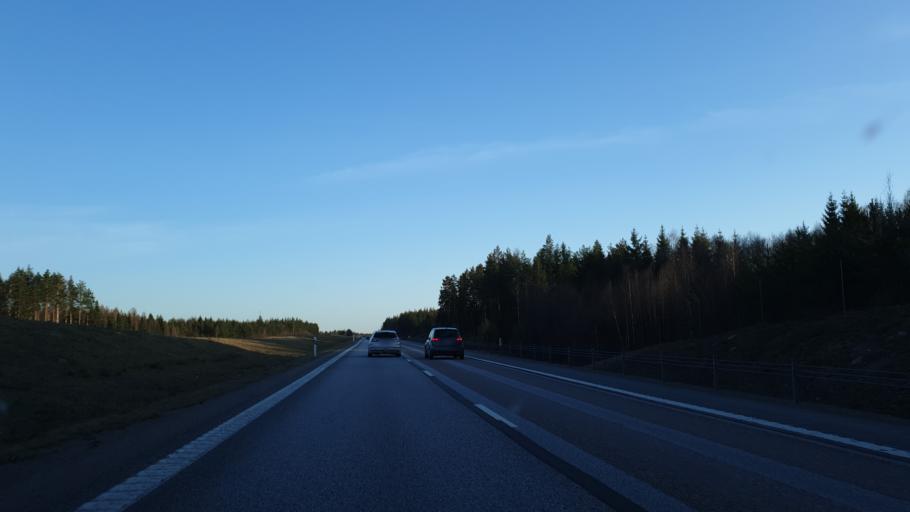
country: SE
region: Uppsala
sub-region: Tierps Kommun
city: Tierp
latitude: 60.2524
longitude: 17.5002
